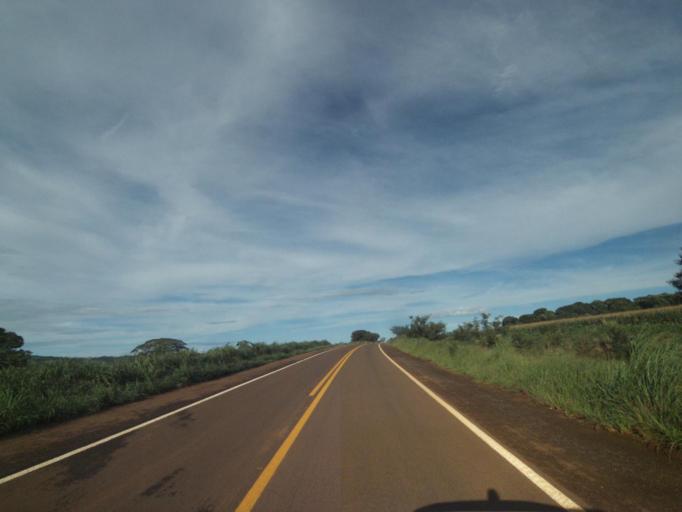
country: BR
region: Goias
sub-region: Jaragua
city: Jaragua
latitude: -15.9067
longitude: -49.5538
